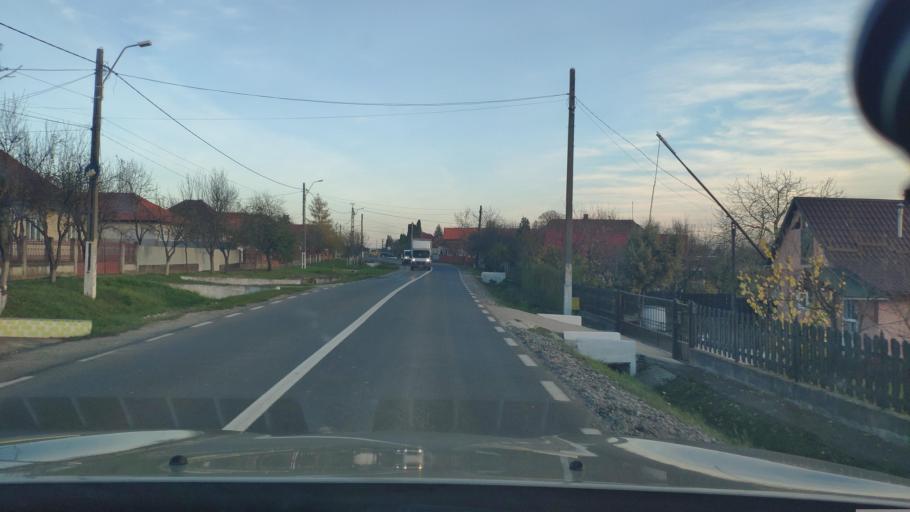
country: RO
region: Satu Mare
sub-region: Comuna Apa
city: Apa
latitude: 47.7659
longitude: 23.1830
